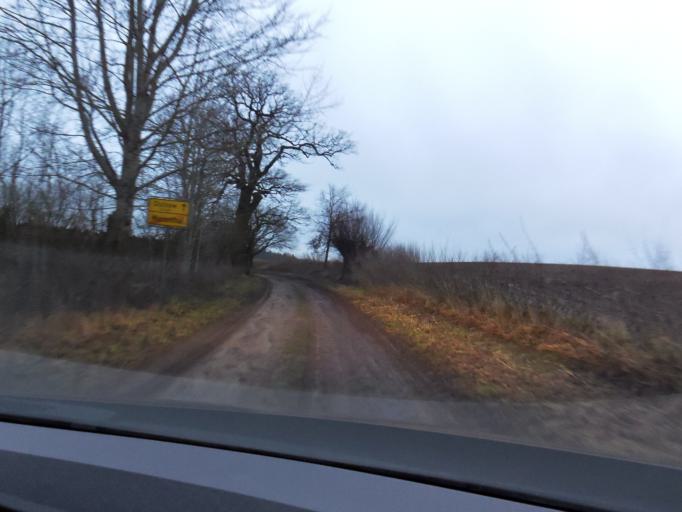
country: DE
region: Mecklenburg-Vorpommern
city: Roggendorf
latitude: 53.6850
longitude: 10.9903
